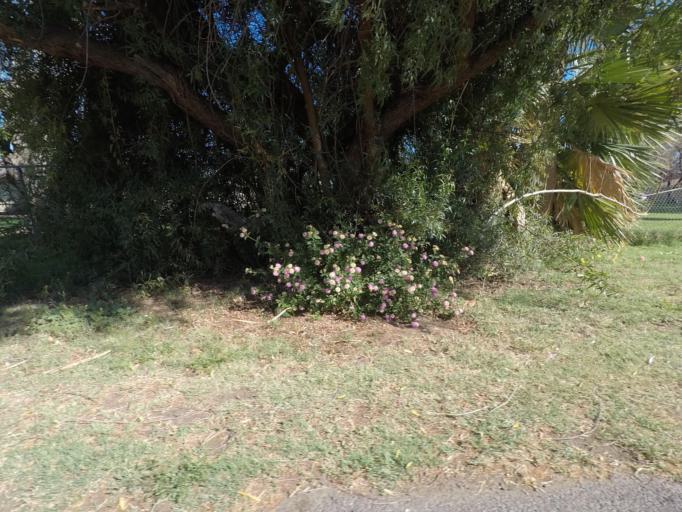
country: US
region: Arizona
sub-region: Maricopa County
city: Glendale
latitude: 33.5459
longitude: -112.1300
